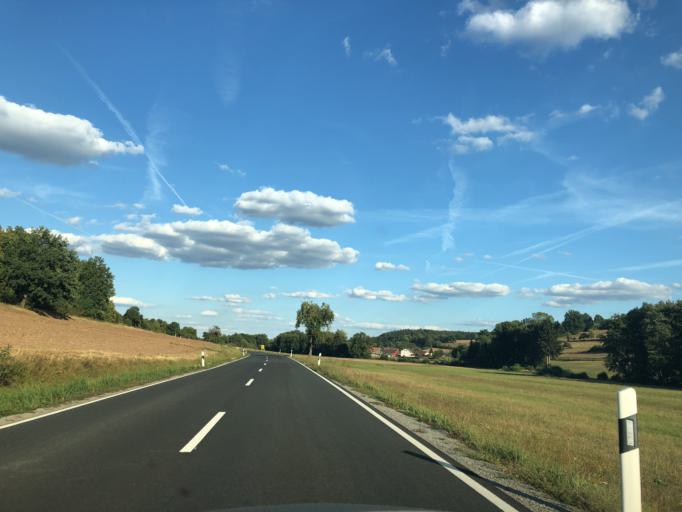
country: DE
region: Bavaria
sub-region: Upper Franconia
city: Burgwindheim
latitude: 49.8325
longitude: 10.5575
